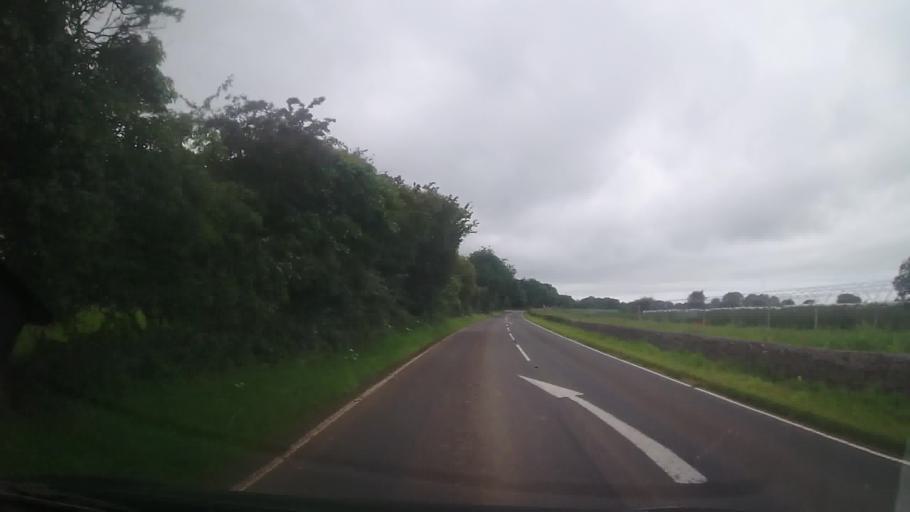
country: GB
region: Wales
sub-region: Gwynedd
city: Y Felinheli
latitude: 53.1971
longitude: -4.2337
